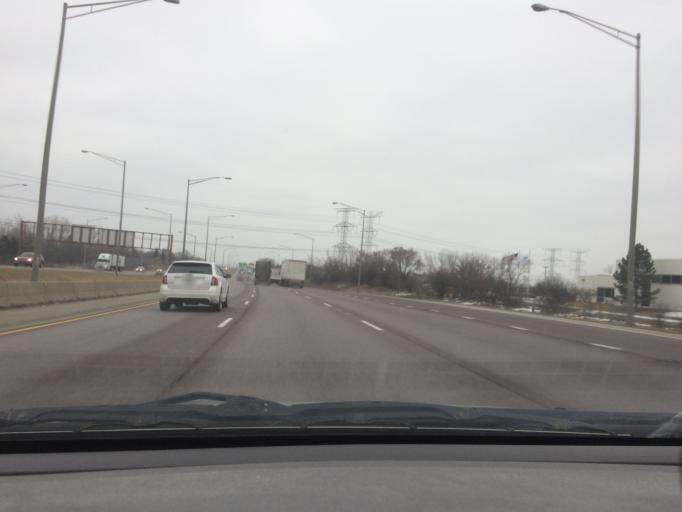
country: US
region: Illinois
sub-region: DuPage County
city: Itasca
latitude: 41.9471
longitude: -88.0376
